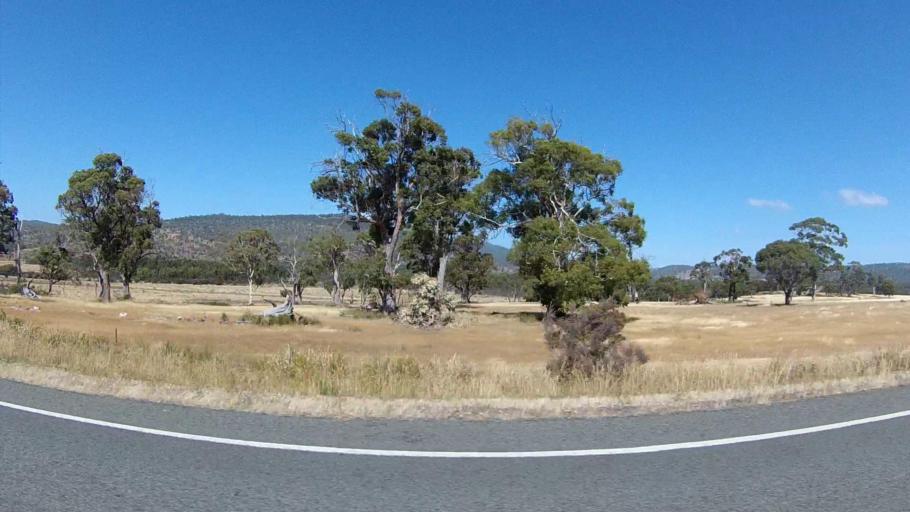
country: AU
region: Tasmania
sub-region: Sorell
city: Sorell
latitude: -42.5946
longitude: 147.7749
